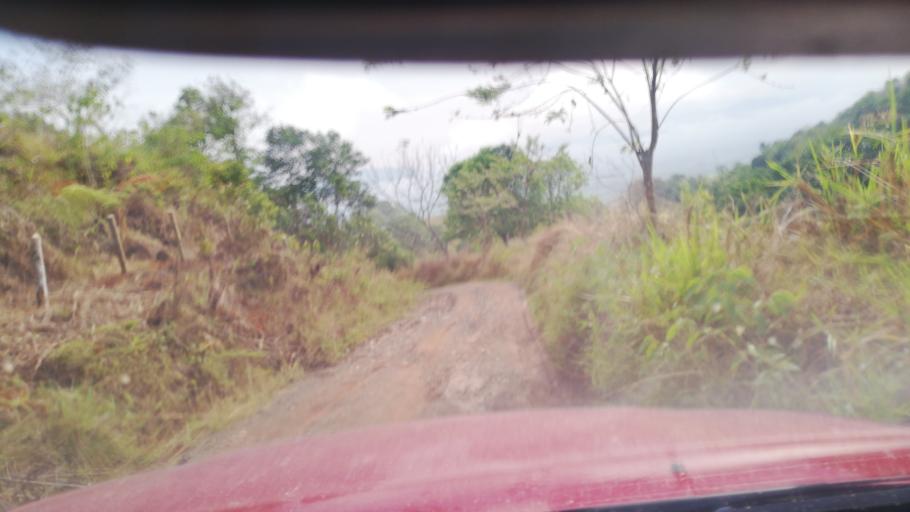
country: CO
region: Risaralda
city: La Virginia
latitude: 4.8762
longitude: -75.9407
